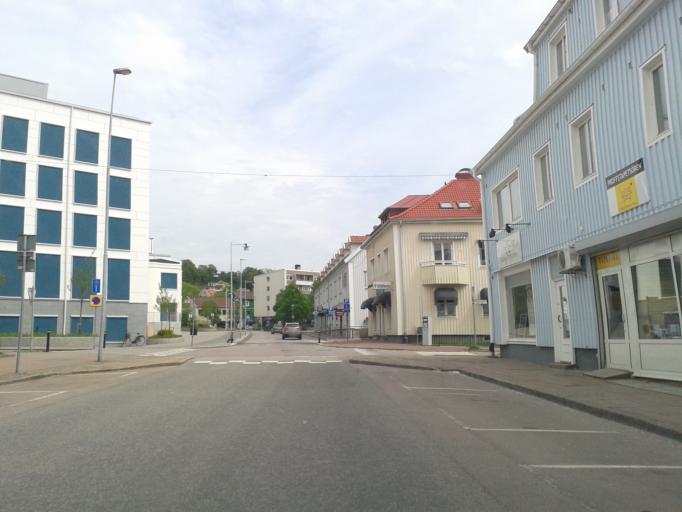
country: SE
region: Vaestra Goetaland
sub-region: Kungalvs Kommun
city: Kungalv
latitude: 57.8707
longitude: 11.9777
